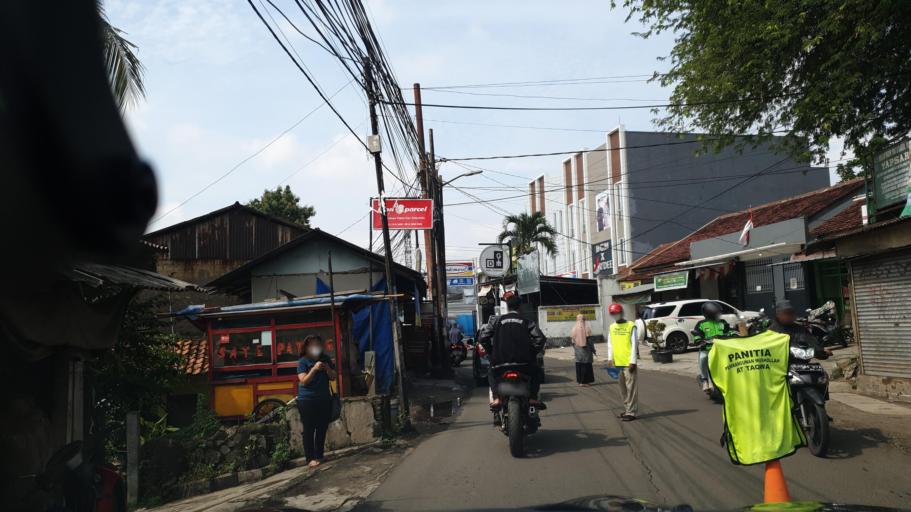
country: ID
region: West Java
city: Pamulang
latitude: -6.3132
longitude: 106.7546
